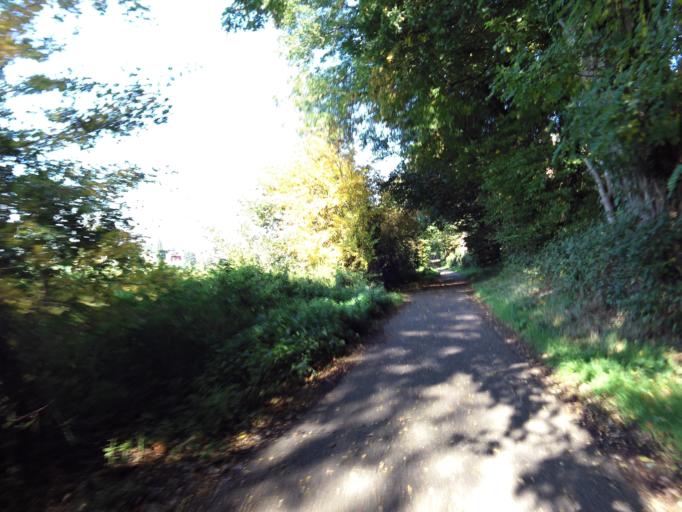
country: DE
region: North Rhine-Westphalia
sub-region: Regierungsbezirk Koln
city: Ubach-Palenberg
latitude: 50.9018
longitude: 6.1128
